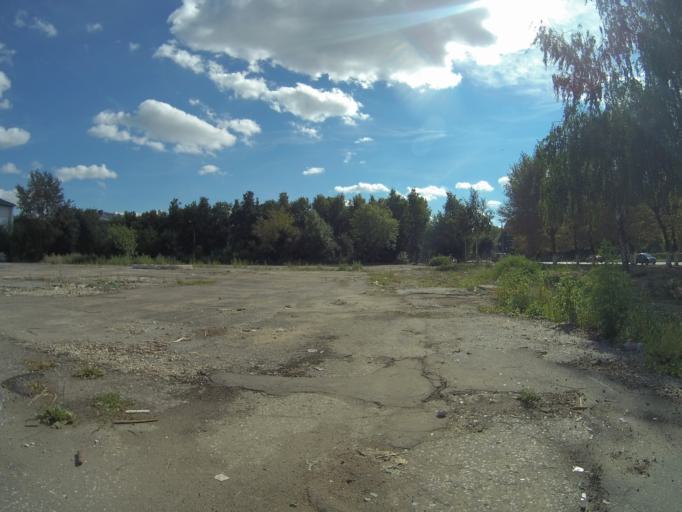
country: RU
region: Vladimir
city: Vladimir
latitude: 56.1392
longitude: 40.3652
